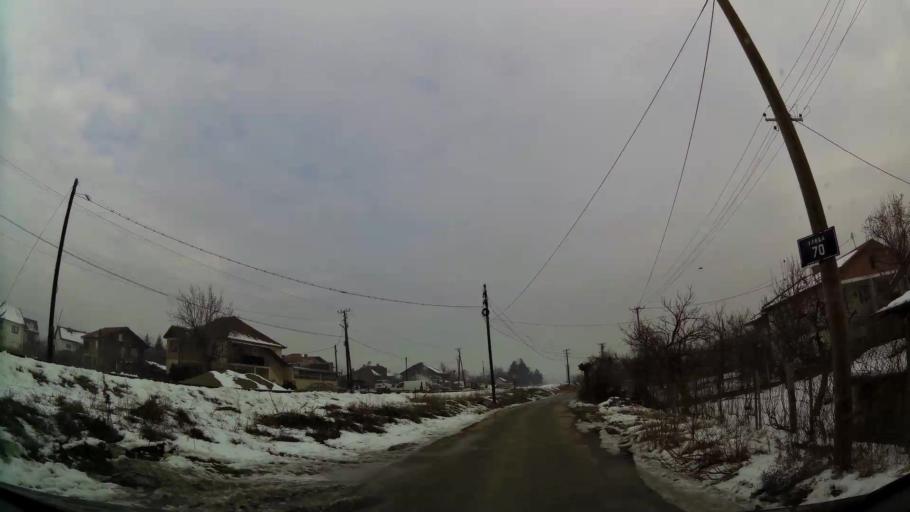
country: MK
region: Saraj
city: Saraj
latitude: 42.0445
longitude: 21.3535
